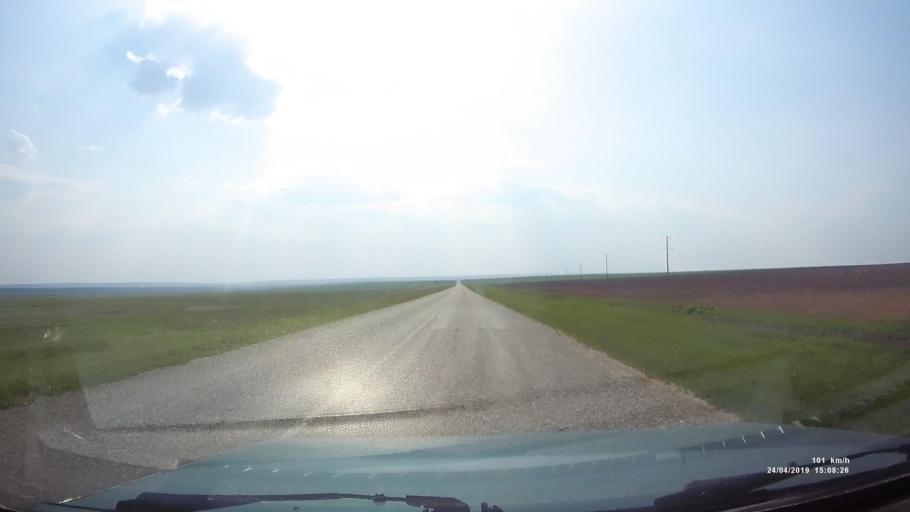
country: RU
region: Rostov
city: Remontnoye
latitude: 46.5597
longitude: 43.3831
